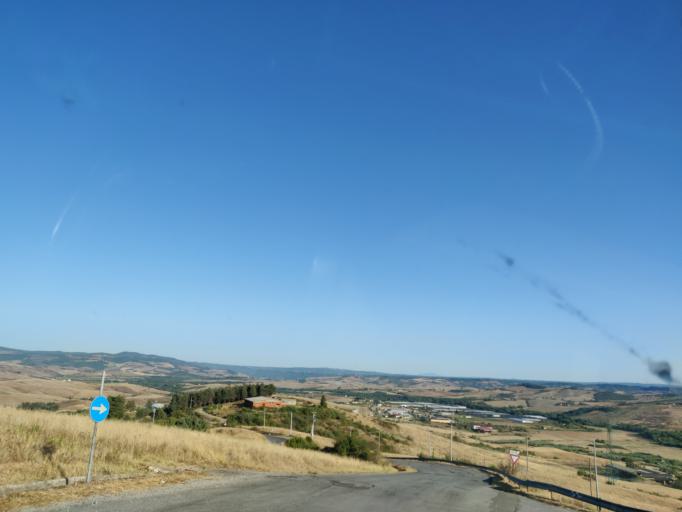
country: IT
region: Tuscany
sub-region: Provincia di Siena
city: Piancastagnaio
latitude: 42.8355
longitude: 11.7103
